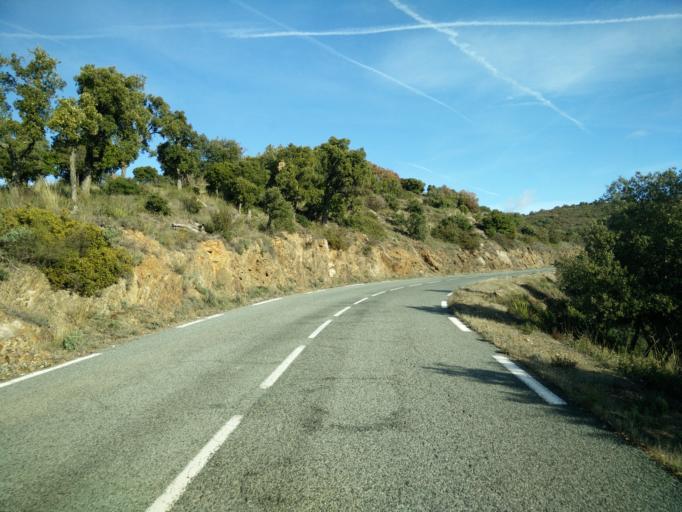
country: FR
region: Provence-Alpes-Cote d'Azur
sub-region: Departement du Var
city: Saint-Raphael
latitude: 43.4947
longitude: 6.7788
